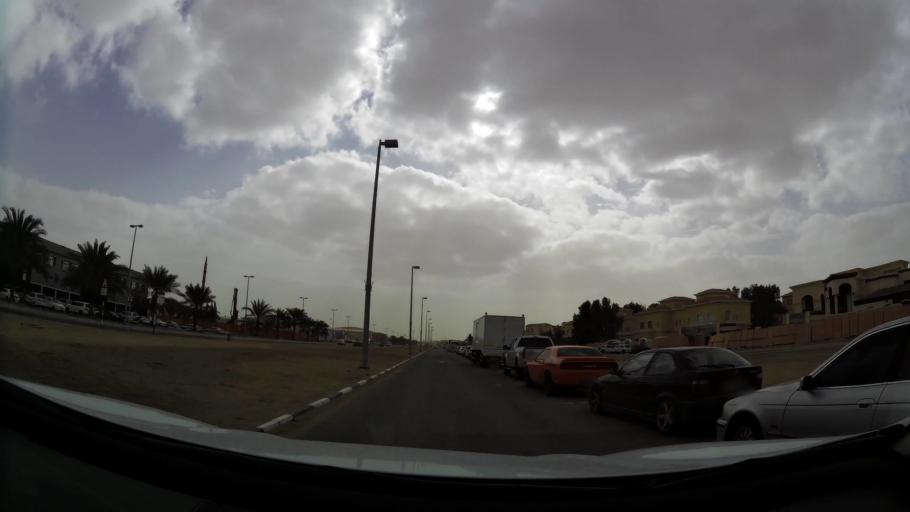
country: AE
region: Abu Dhabi
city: Abu Dhabi
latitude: 24.4159
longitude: 54.4947
